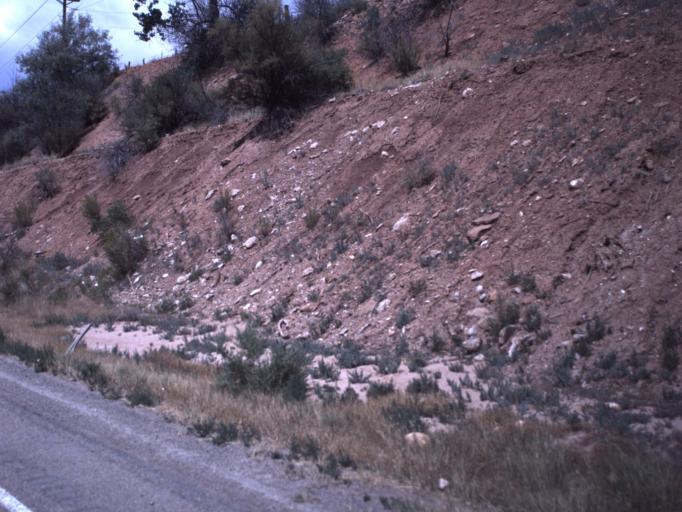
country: US
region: Utah
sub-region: Duchesne County
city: Roosevelt
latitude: 40.3021
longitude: -109.9153
